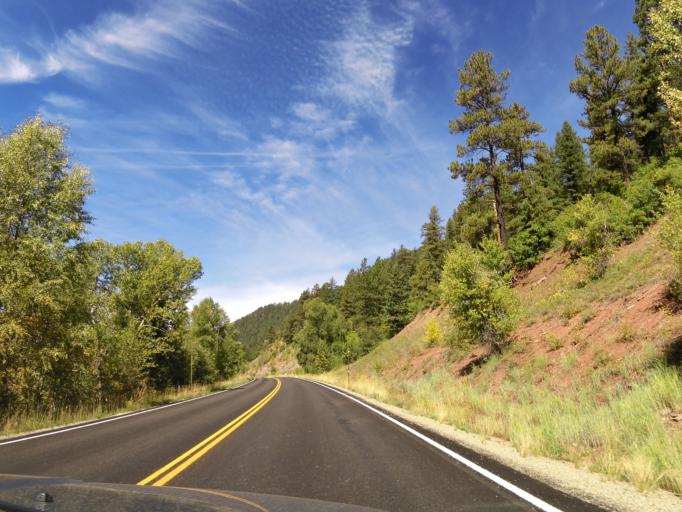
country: US
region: Colorado
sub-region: Montezuma County
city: Mancos
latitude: 37.5783
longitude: -108.2078
